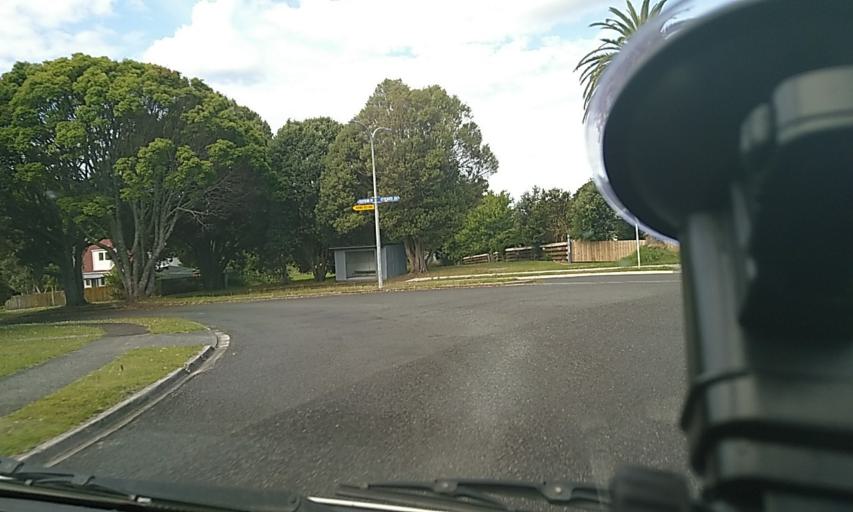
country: NZ
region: Bay of Plenty
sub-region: Western Bay of Plenty District
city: Waihi Beach
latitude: -37.4453
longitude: 175.9621
